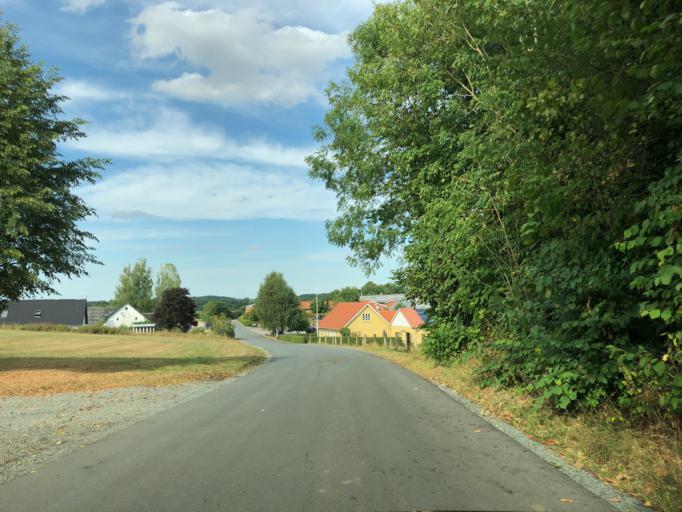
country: DK
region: South Denmark
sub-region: Vejle Kommune
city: Egtved
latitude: 55.6701
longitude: 9.2670
